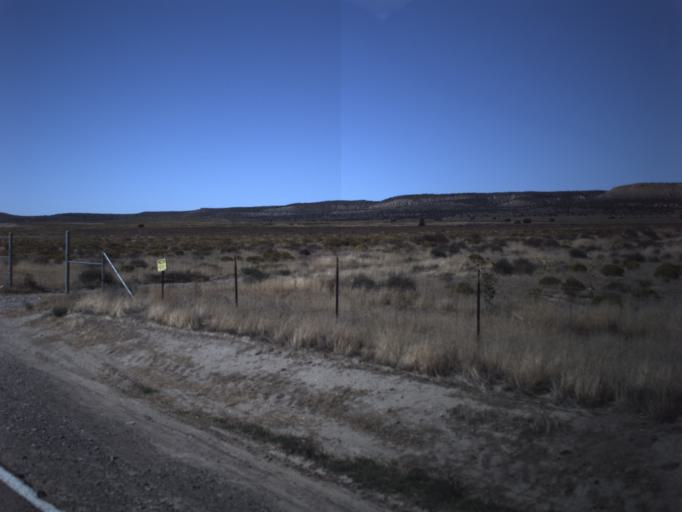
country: US
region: Utah
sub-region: Utah County
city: Eagle Mountain
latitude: 40.1734
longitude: -111.9305
